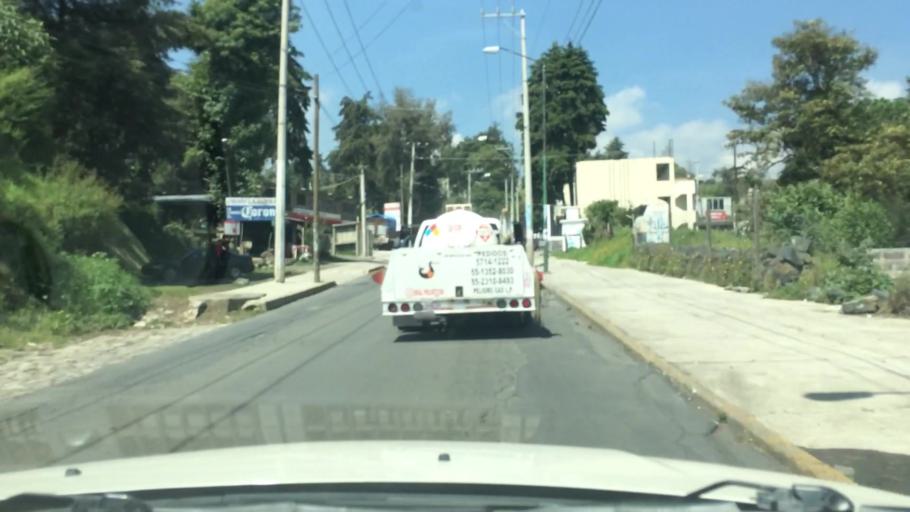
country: MX
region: Mexico City
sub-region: Tlalpan
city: Lomas de Tepemecatl
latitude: 19.2342
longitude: -99.1855
